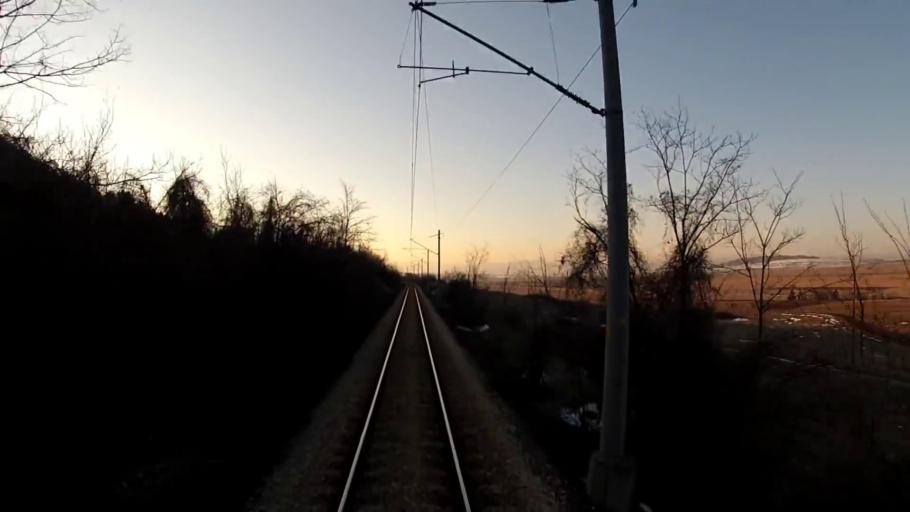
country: BG
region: Sofiya
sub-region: Obshtina Dragoman
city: Dragoman
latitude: 42.9007
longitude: 22.9508
